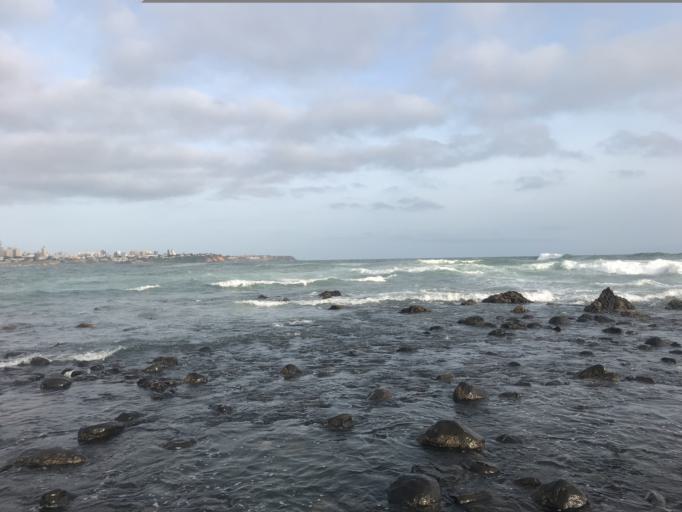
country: SN
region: Dakar
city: Dakar
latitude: 14.6746
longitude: -17.4687
